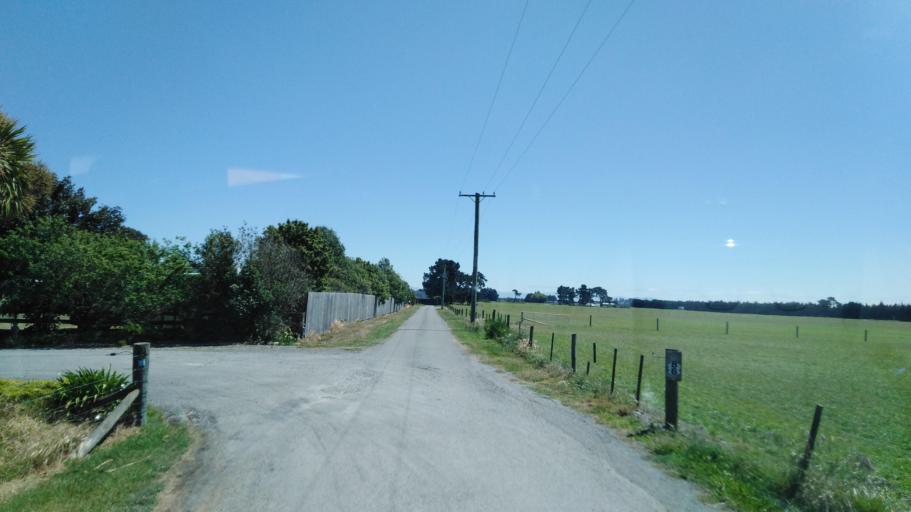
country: NZ
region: Canterbury
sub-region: Selwyn District
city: Rolleston
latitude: -43.5636
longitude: 172.4381
